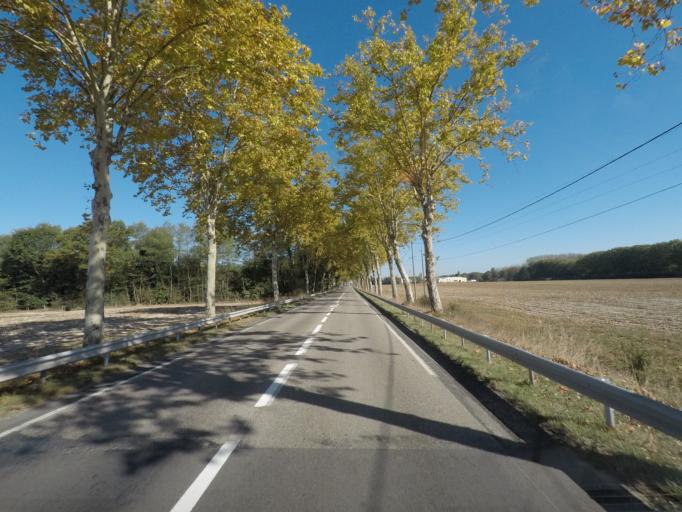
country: FR
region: Rhone-Alpes
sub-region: Departement de l'Ain
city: Servas
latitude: 46.1205
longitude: 5.1558
